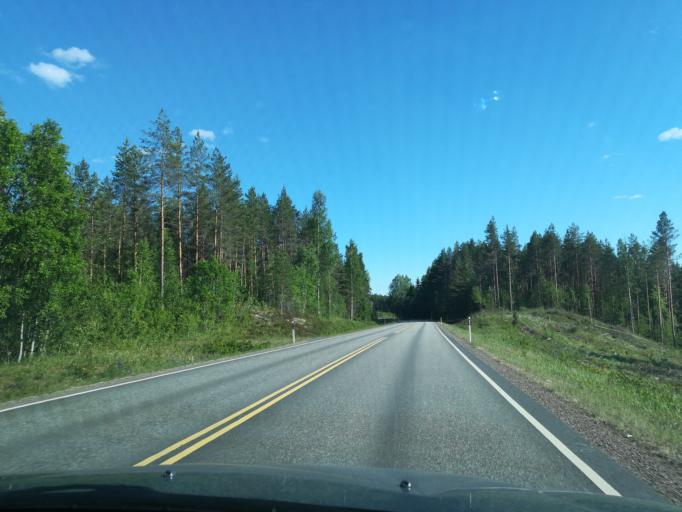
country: FI
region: South Karelia
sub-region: Imatra
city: Ruokolahti
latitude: 61.3954
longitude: 28.6348
